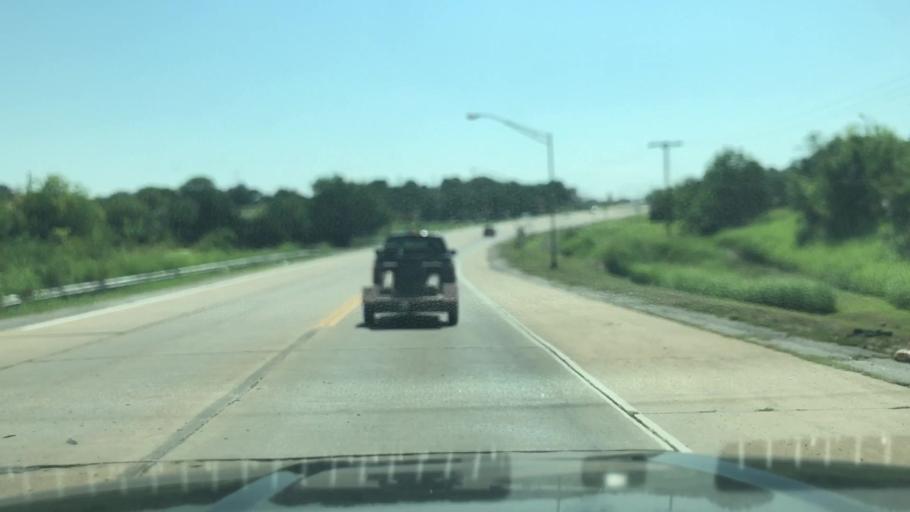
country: US
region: Oklahoma
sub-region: Creek County
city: Drumright
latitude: 35.9884
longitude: -96.5891
